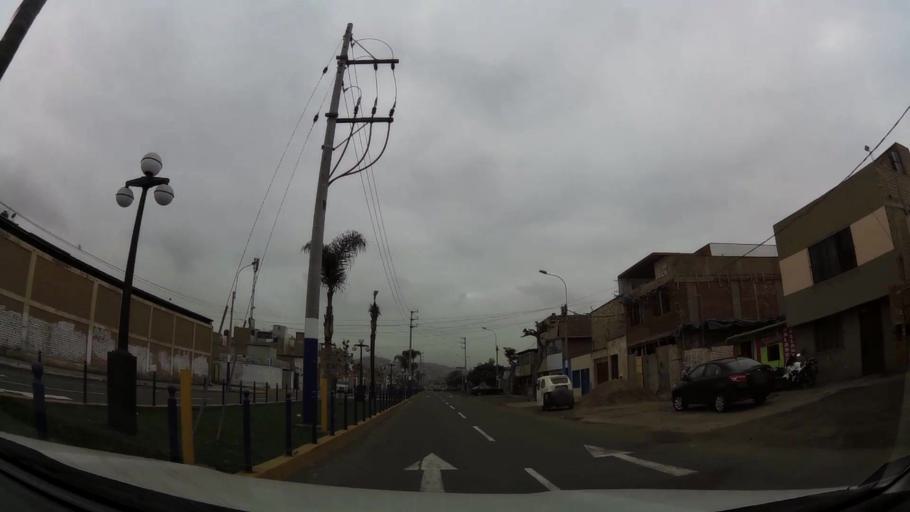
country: PE
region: Lima
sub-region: Lima
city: Surco
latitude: -12.2035
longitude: -77.0072
